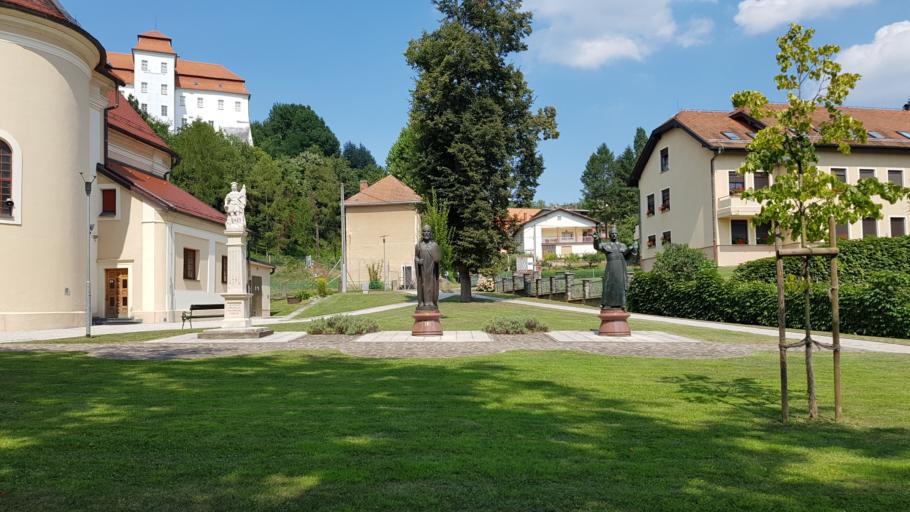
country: SI
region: Lendava-Lendva
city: Lendava
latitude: 46.5655
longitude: 16.4519
